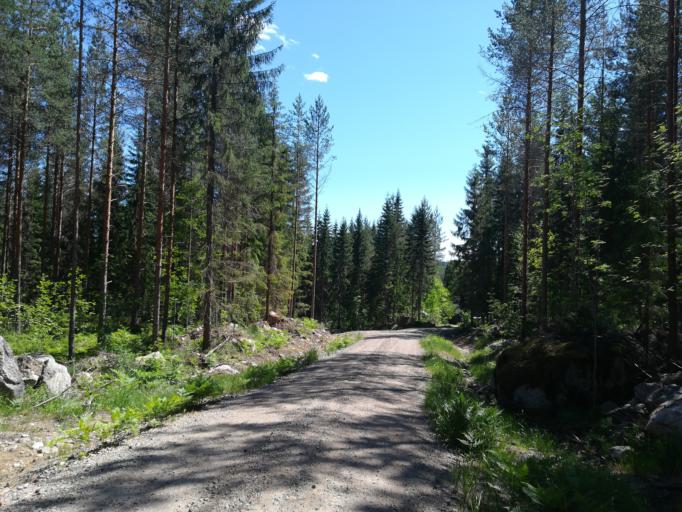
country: FI
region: Southern Savonia
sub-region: Mikkeli
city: Puumala
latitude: 61.6155
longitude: 28.1683
